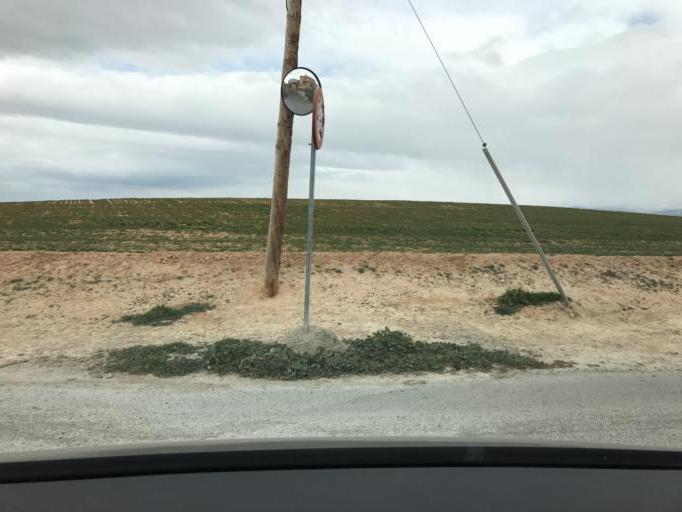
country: ES
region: Andalusia
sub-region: Provincia de Granada
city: Cullar-Vega
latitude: 37.1378
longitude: -3.6729
